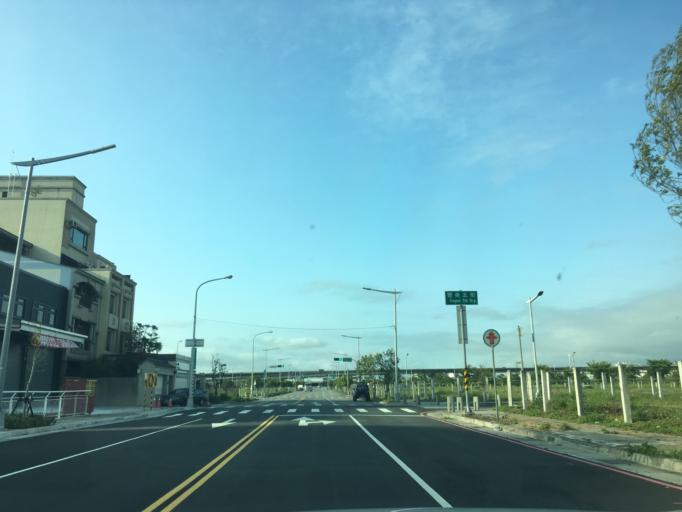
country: TW
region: Taiwan
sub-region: Taichung City
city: Taichung
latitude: 24.1956
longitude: 120.6906
